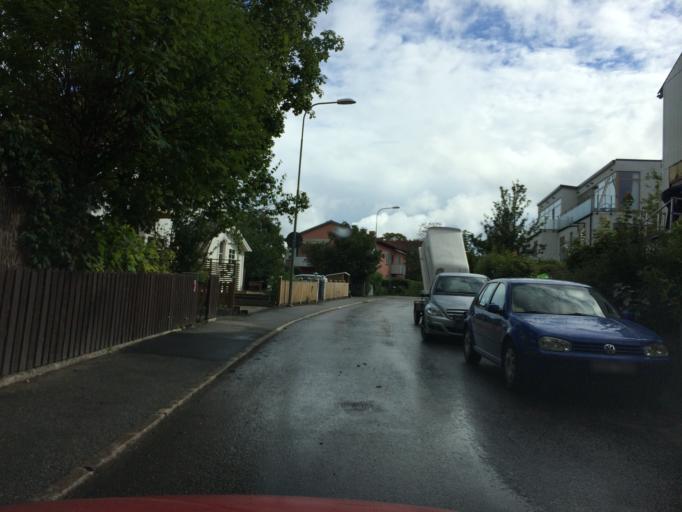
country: SE
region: Stockholm
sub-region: Huddinge Kommun
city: Segeltorp
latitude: 59.3025
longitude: 17.9558
